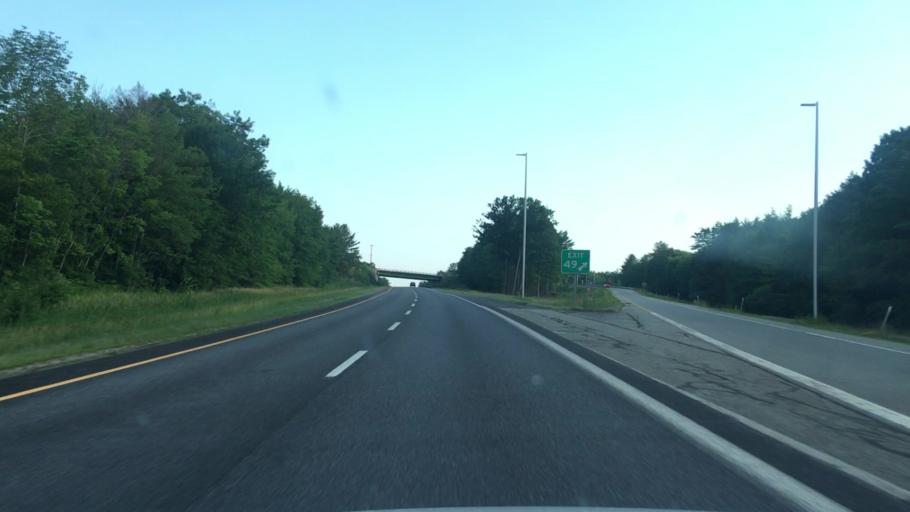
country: US
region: Maine
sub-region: Kennebec County
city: Gardiner
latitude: 44.1818
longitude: -69.8337
